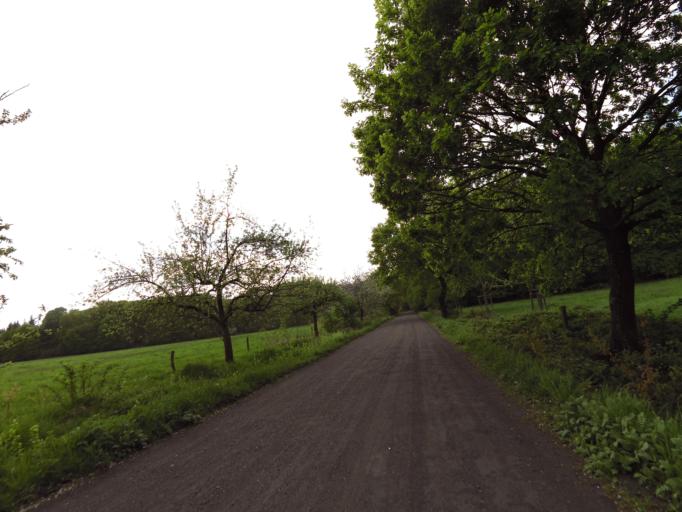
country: DE
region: North Rhine-Westphalia
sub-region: Regierungsbezirk Koln
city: Bonn
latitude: 50.6838
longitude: 7.0934
